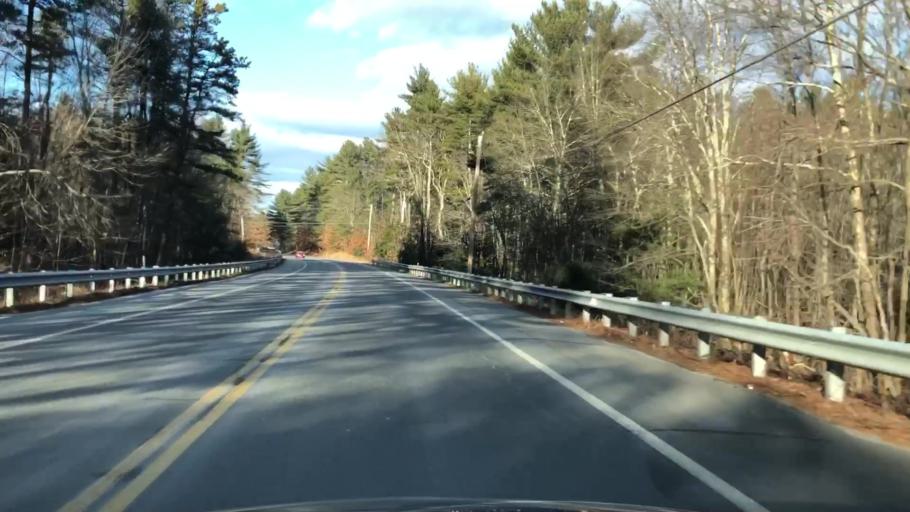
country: US
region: New Hampshire
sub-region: Hillsborough County
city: Brookline
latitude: 42.7155
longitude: -71.6627
